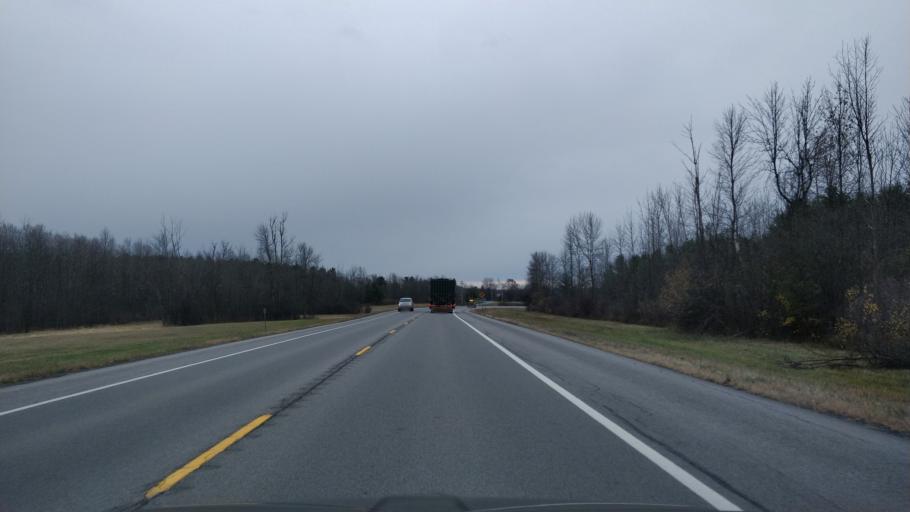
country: CA
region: Ontario
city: Brockville
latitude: 44.5867
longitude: -75.6399
